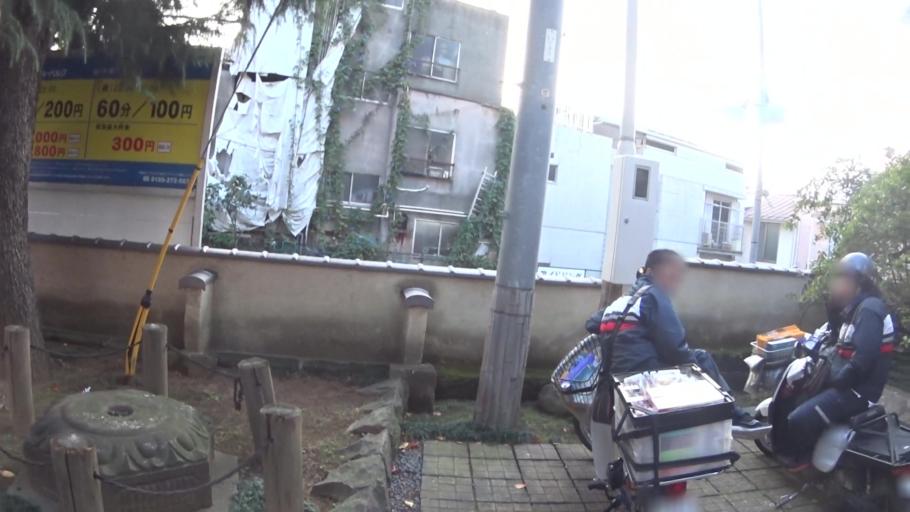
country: JP
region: Tokyo
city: Tokyo
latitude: 35.7193
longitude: 139.7671
